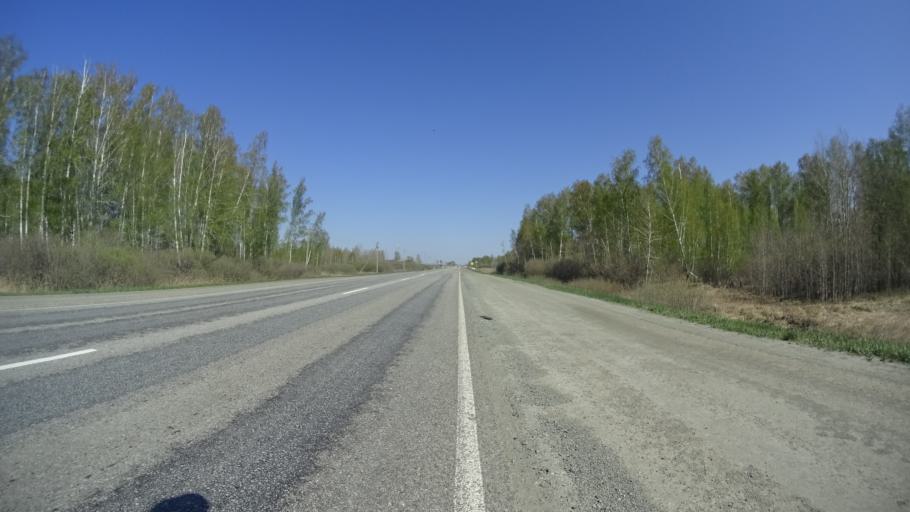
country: RU
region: Chelyabinsk
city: Troitsk
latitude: 54.1840
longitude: 61.4344
